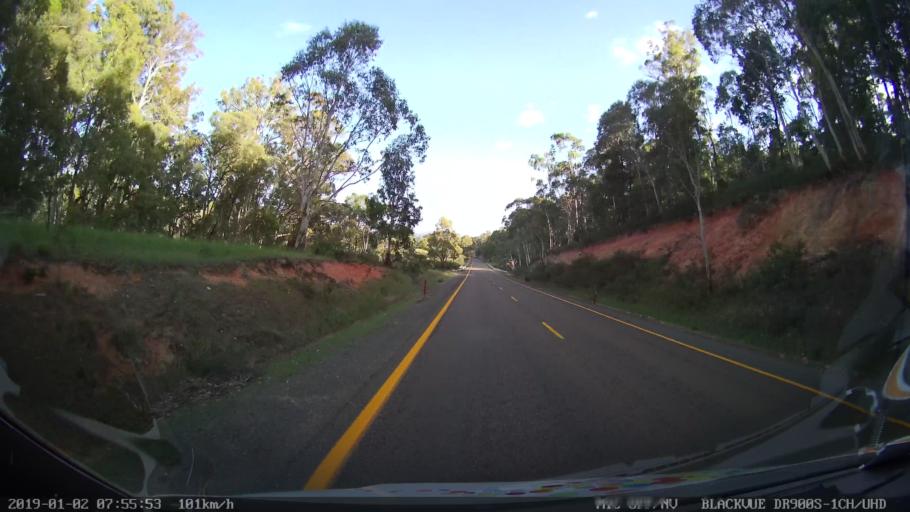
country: AU
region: New South Wales
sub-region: Tumut Shire
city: Tumut
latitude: -35.6779
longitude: 148.4862
